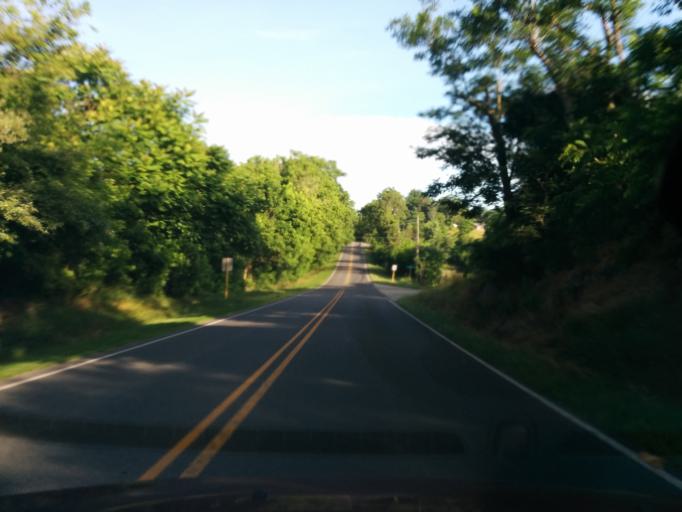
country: US
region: Virginia
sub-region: City of Lexington
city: Lexington
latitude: 37.8019
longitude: -79.4644
